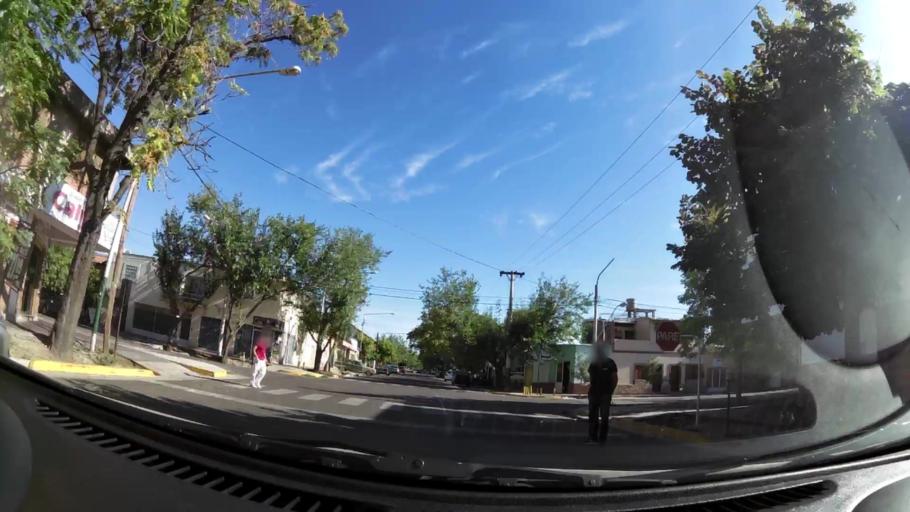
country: AR
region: Mendoza
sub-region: Departamento de Godoy Cruz
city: Godoy Cruz
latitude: -32.9093
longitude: -68.8333
